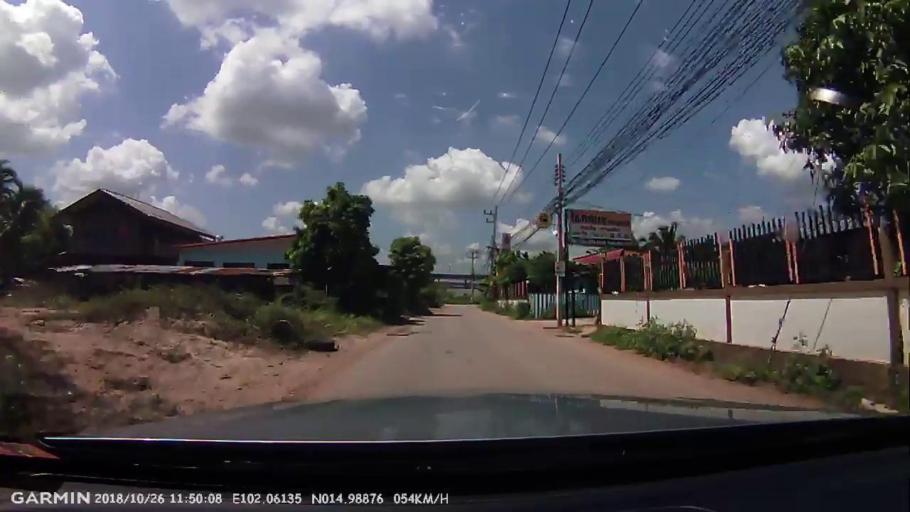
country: TH
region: Nakhon Ratchasima
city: Nakhon Ratchasima
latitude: 14.9888
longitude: 102.0612
